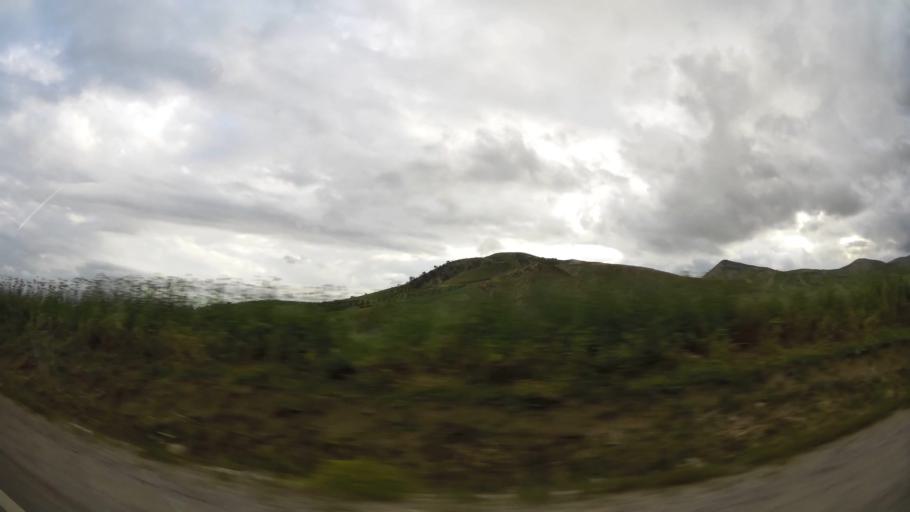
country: MA
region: Taza-Al Hoceima-Taounate
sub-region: Taza
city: Taza
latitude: 34.2873
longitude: -3.9630
